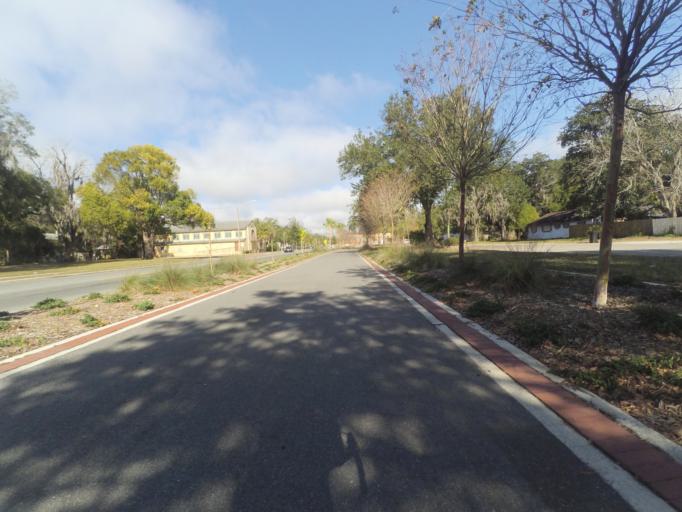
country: US
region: Florida
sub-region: Alachua County
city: Gainesville
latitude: 29.6565
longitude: -82.3307
